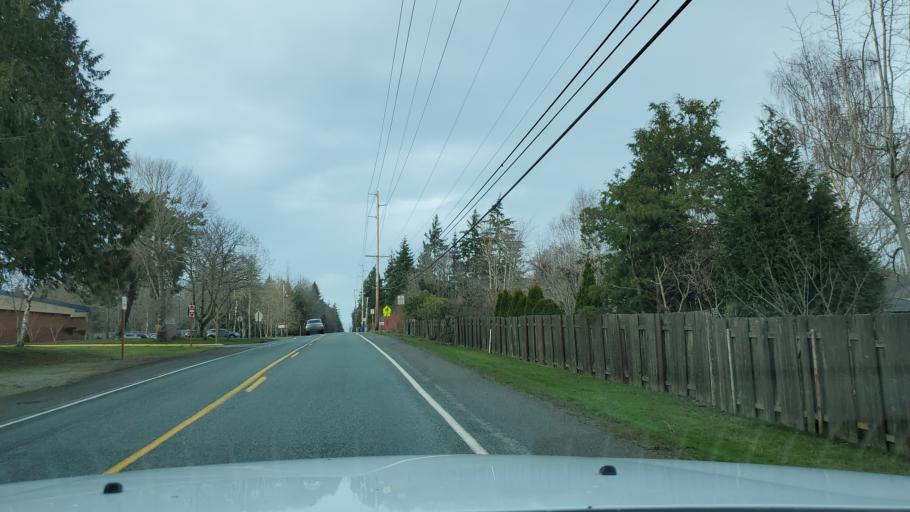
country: US
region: Washington
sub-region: Skagit County
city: Anacortes
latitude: 48.4456
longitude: -122.5816
